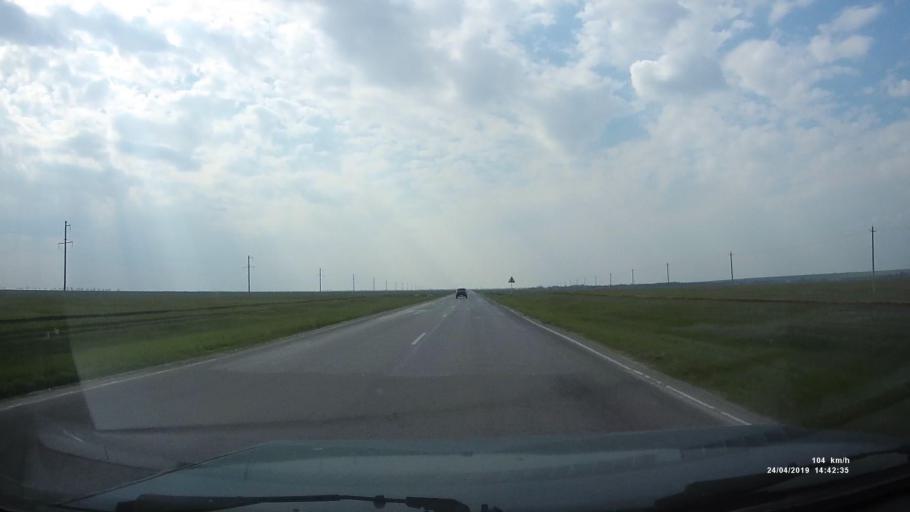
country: RU
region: Rostov
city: Remontnoye
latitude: 46.4529
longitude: 43.8587
